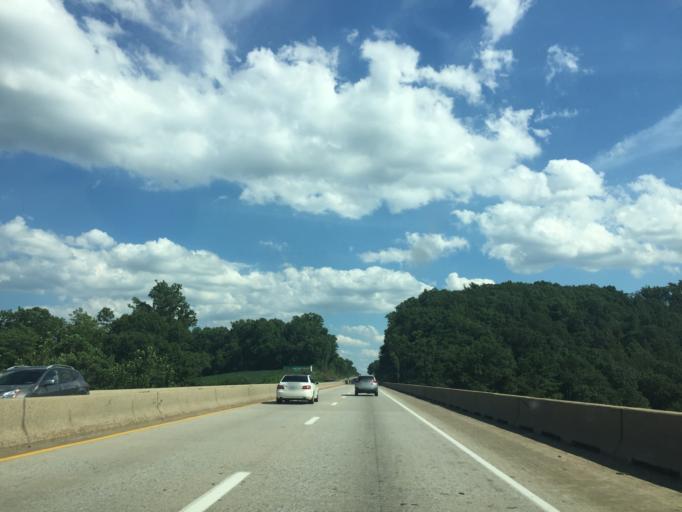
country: US
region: Pennsylvania
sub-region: York County
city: Valley Green
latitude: 40.1031
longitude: -76.7790
